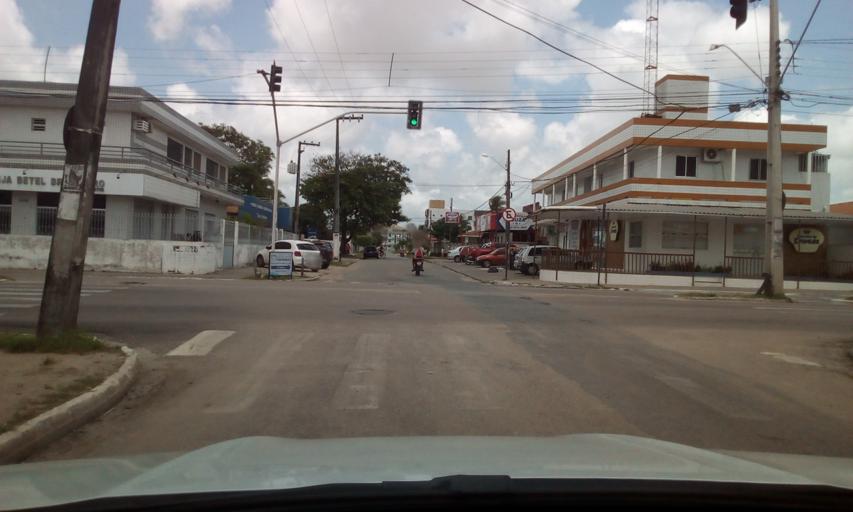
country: BR
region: Paraiba
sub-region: Joao Pessoa
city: Joao Pessoa
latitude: -7.1622
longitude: -34.8692
